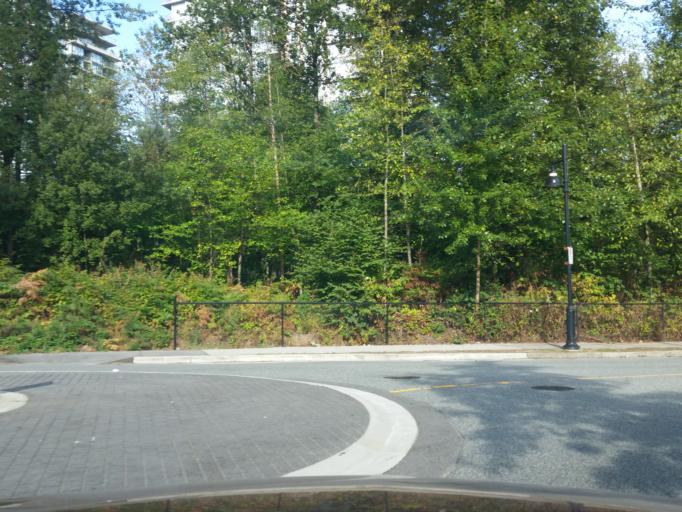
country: CA
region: British Columbia
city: Port Moody
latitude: 49.2787
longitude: -122.8310
